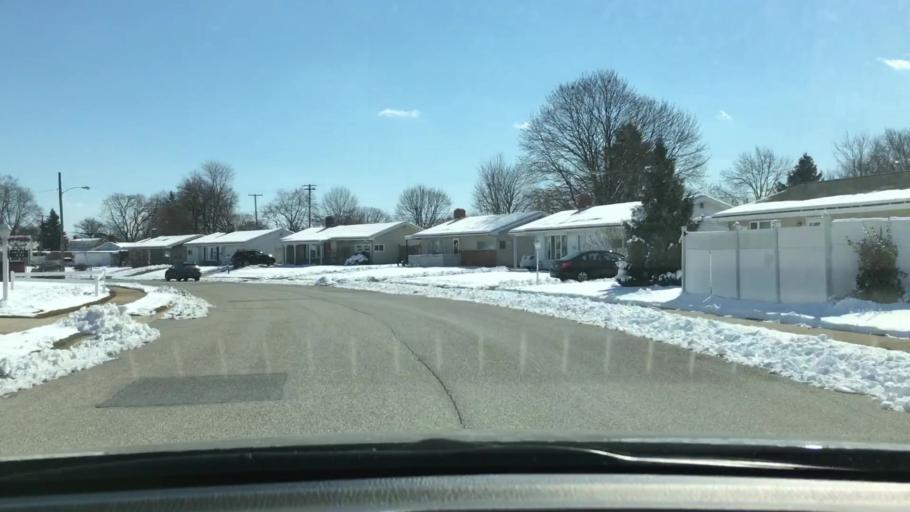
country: US
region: Pennsylvania
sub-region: York County
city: North York
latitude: 39.9766
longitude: -76.7501
